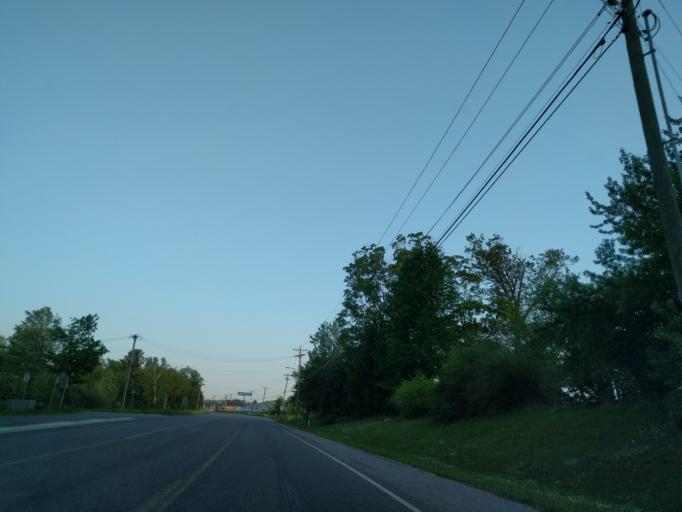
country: US
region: Michigan
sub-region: Marquette County
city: Trowbridge Park
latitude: 46.5549
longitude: -87.4584
